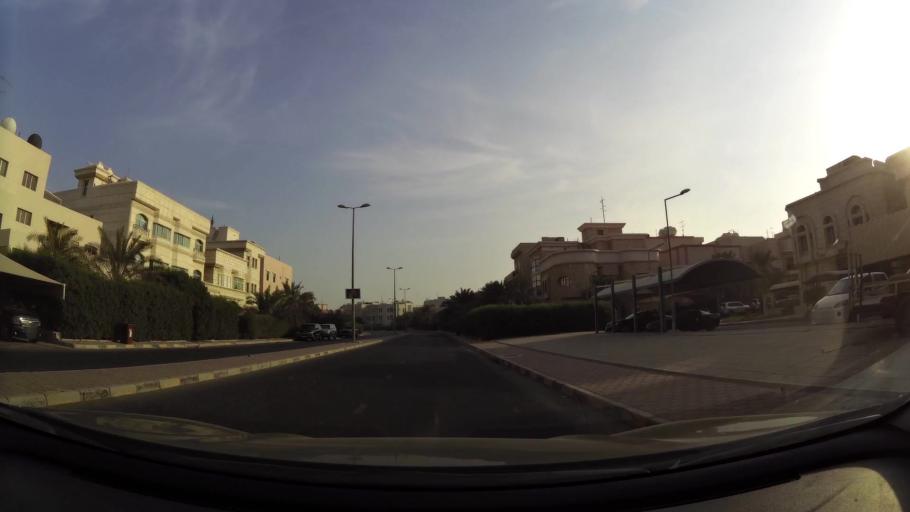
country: KW
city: Al Funaytis
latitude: 29.2334
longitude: 48.0783
